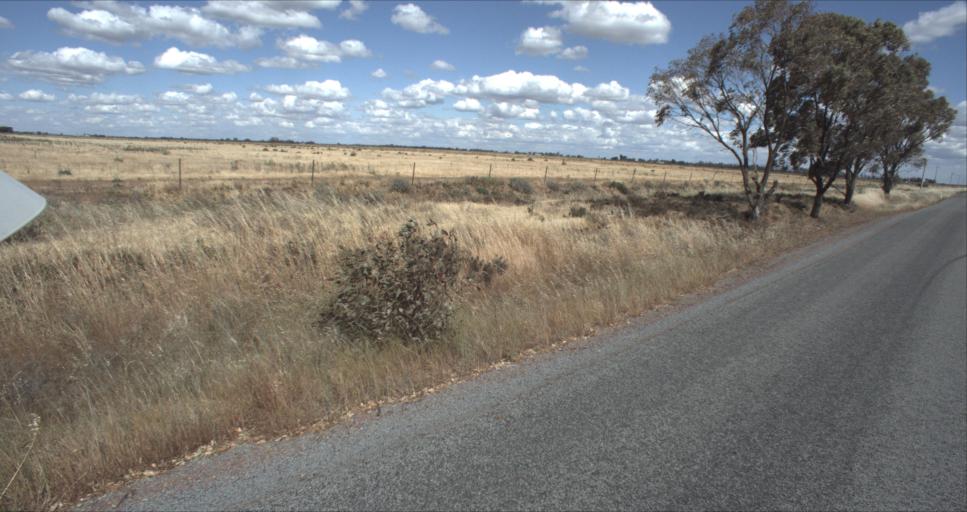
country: AU
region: New South Wales
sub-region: Leeton
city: Leeton
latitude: -34.4935
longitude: 146.2468
